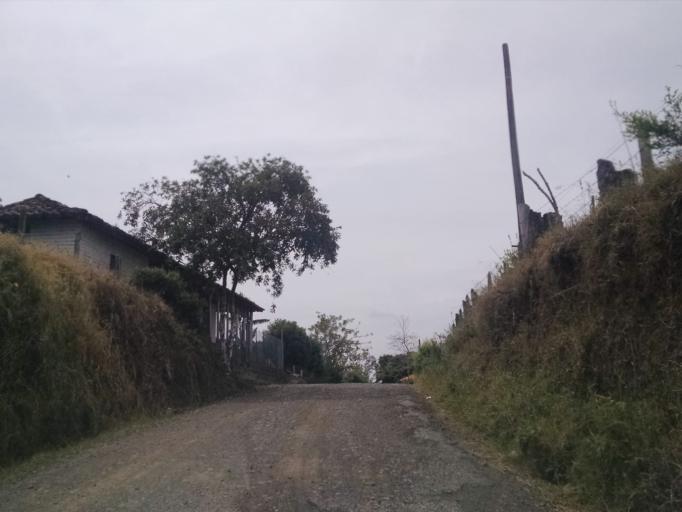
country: CO
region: Valle del Cauca
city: Ulloa
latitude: 4.7192
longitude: -75.7227
